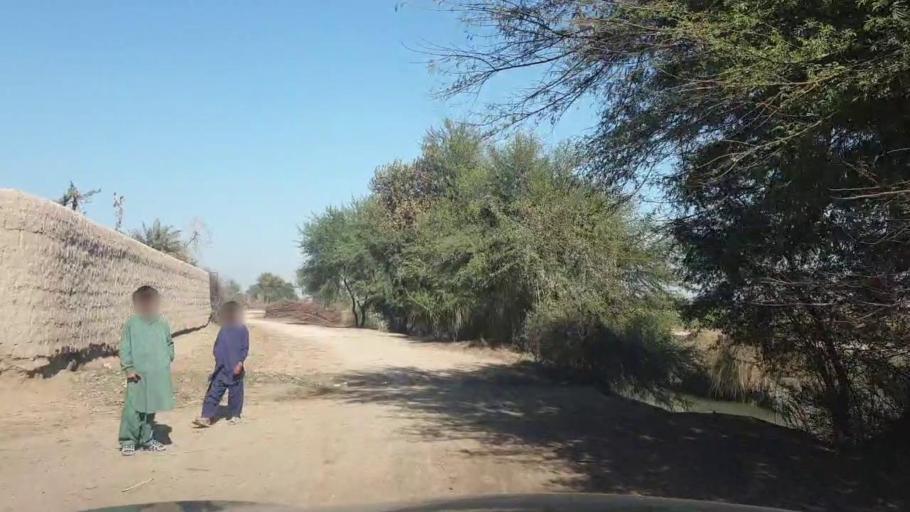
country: PK
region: Sindh
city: Ghotki
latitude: 27.9763
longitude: 69.4191
